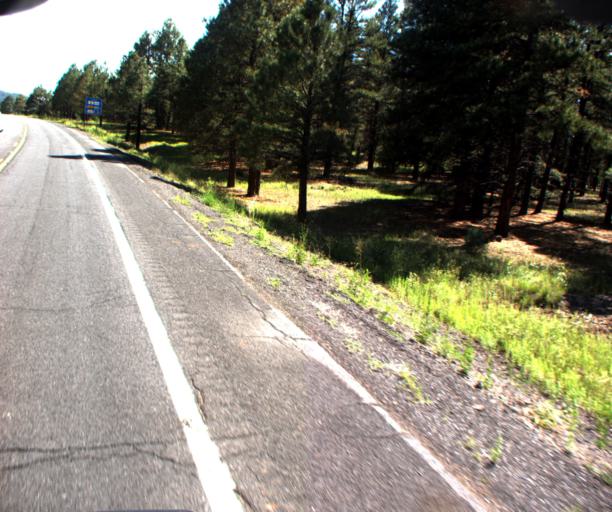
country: US
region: Arizona
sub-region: Coconino County
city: Williams
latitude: 35.2658
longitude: -112.1502
